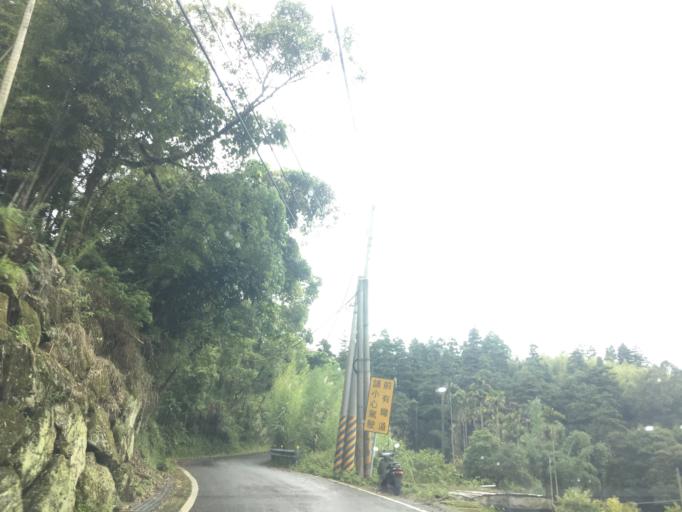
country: TW
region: Taiwan
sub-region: Yunlin
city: Douliu
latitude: 23.5536
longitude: 120.6711
